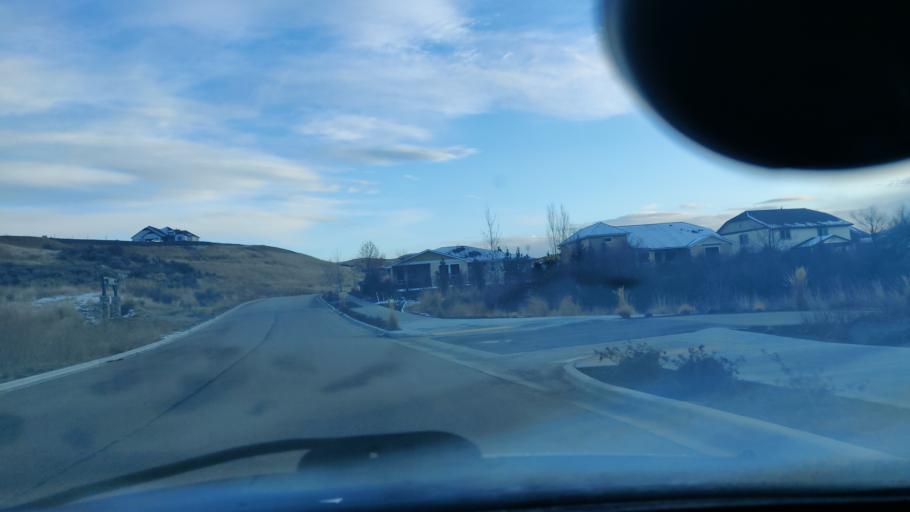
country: US
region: Idaho
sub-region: Ada County
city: Eagle
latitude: 43.7772
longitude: -116.2622
